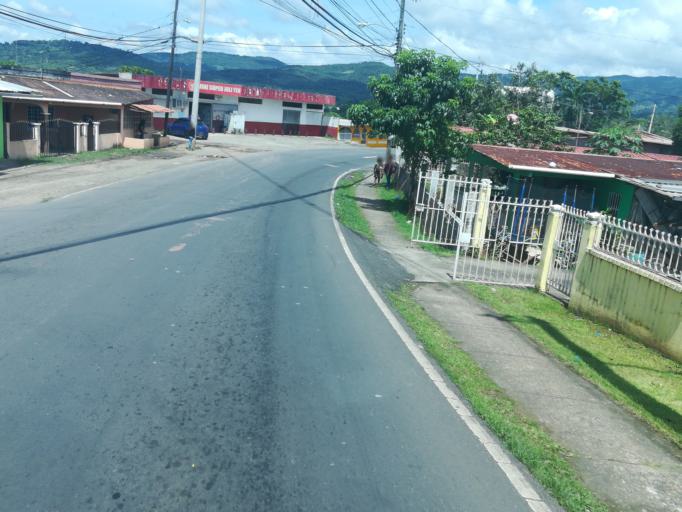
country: PA
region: Panama
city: Tocumen
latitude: 9.0909
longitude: -79.4071
